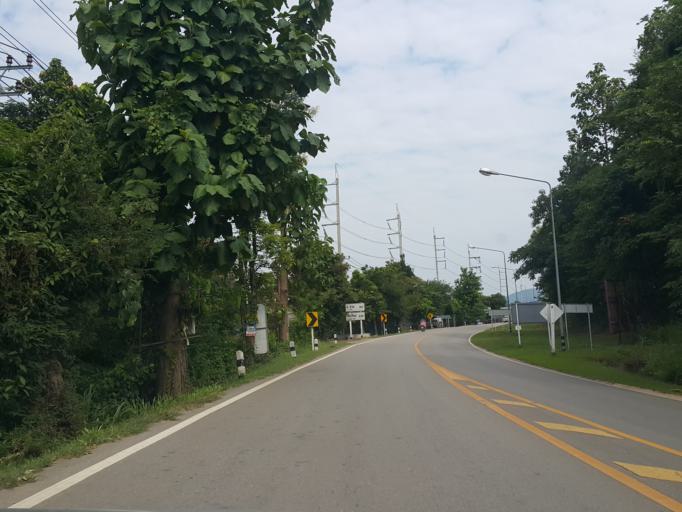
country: TH
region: Mae Hong Son
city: Mae Hong Son
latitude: 19.3496
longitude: 97.9616
